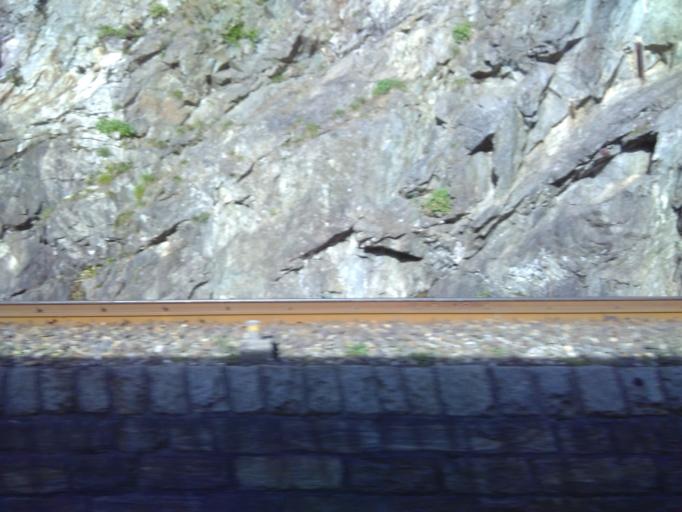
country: CH
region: Ticino
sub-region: Locarno District
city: Losone
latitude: 46.1772
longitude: 8.7635
